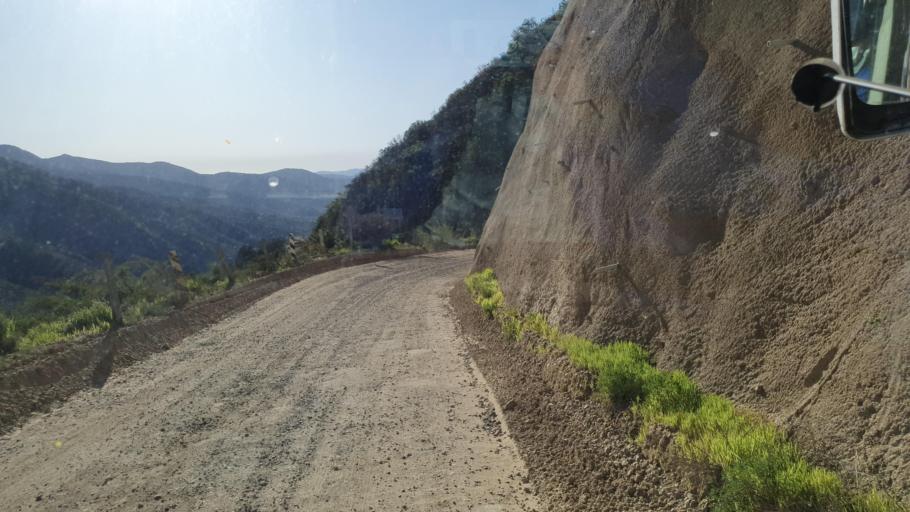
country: CL
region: Valparaiso
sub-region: Provincia de Marga Marga
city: Limache
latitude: -33.2013
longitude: -71.2602
